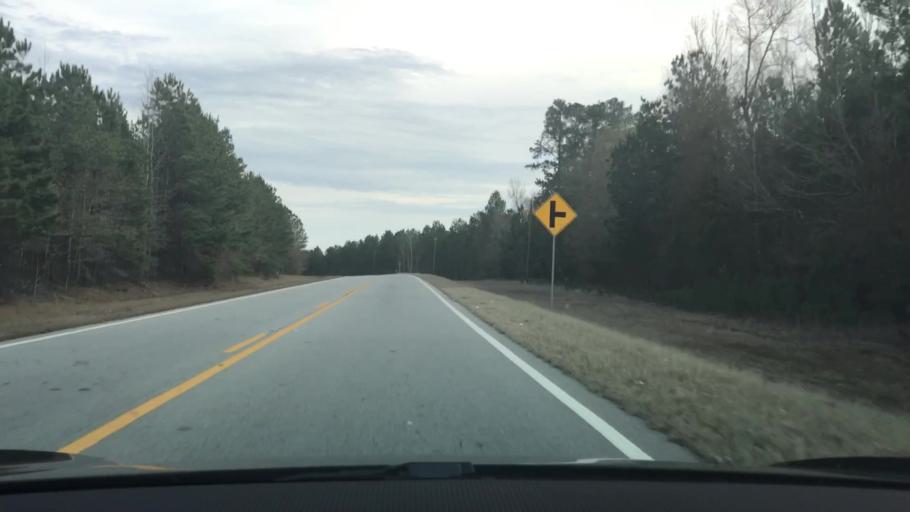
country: US
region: Georgia
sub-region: Glascock County
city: Gibson
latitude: 33.2674
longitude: -82.4932
